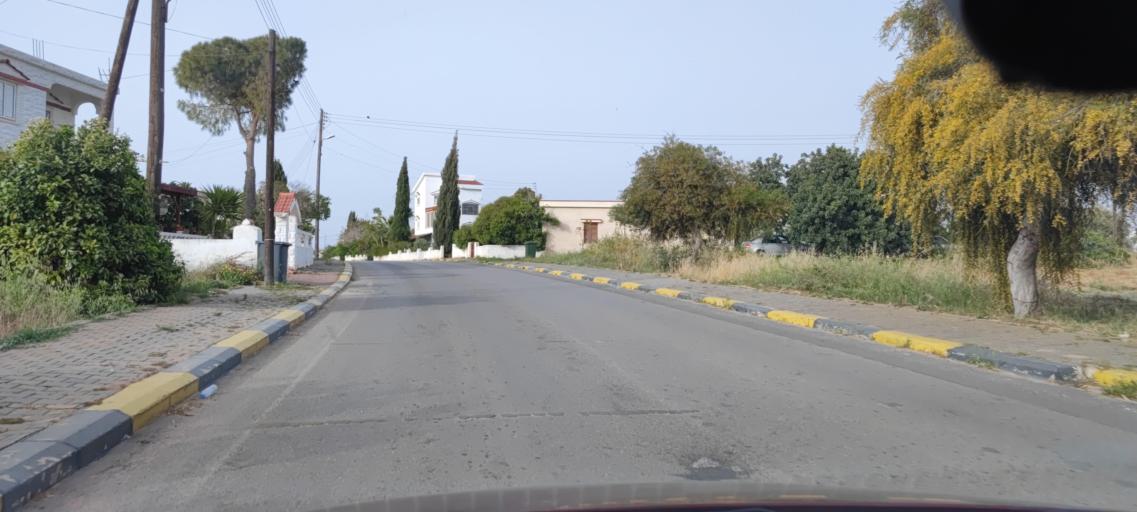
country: CY
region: Ammochostos
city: Leonarisso
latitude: 35.5295
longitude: 34.1848
